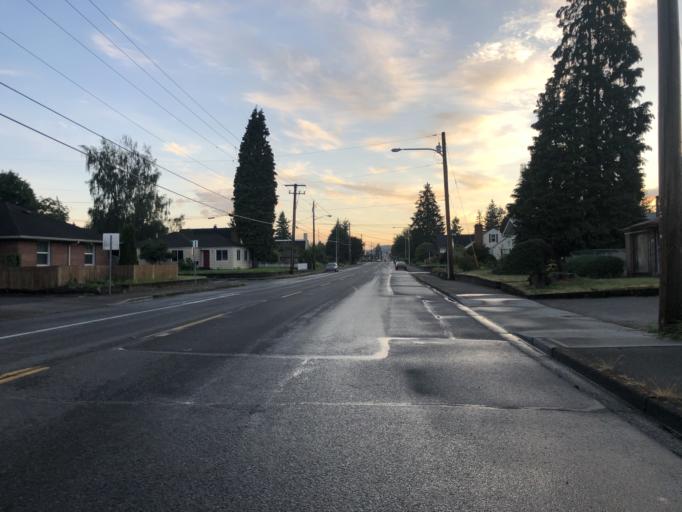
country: US
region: Washington
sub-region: King County
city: Auburn
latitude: 47.3083
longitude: -122.2082
